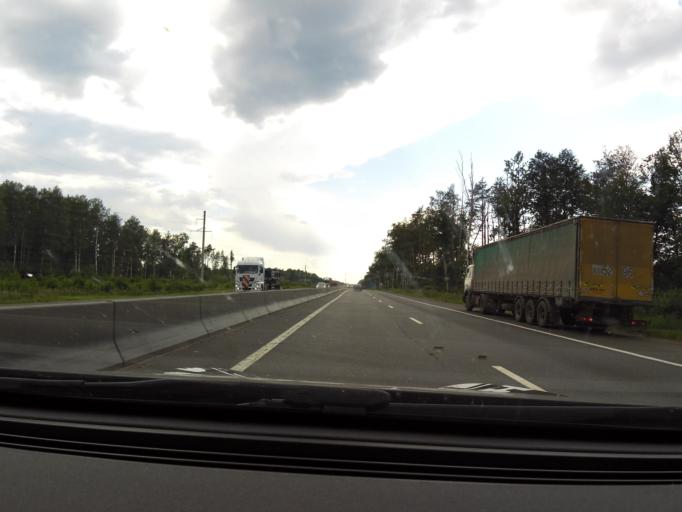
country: RU
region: Nizjnij Novgorod
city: Smolino
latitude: 56.2826
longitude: 43.1121
